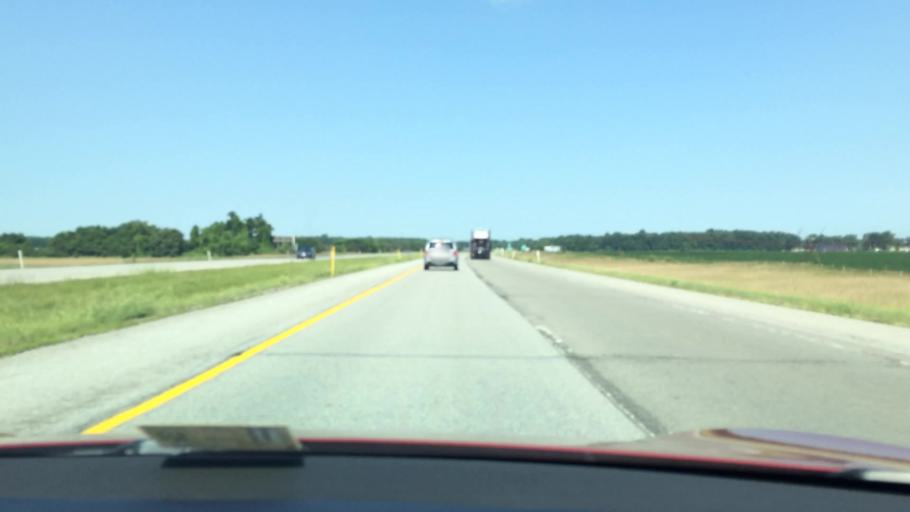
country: US
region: Michigan
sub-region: Saint Joseph County
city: White Pigeon
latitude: 41.7519
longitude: -85.6280
